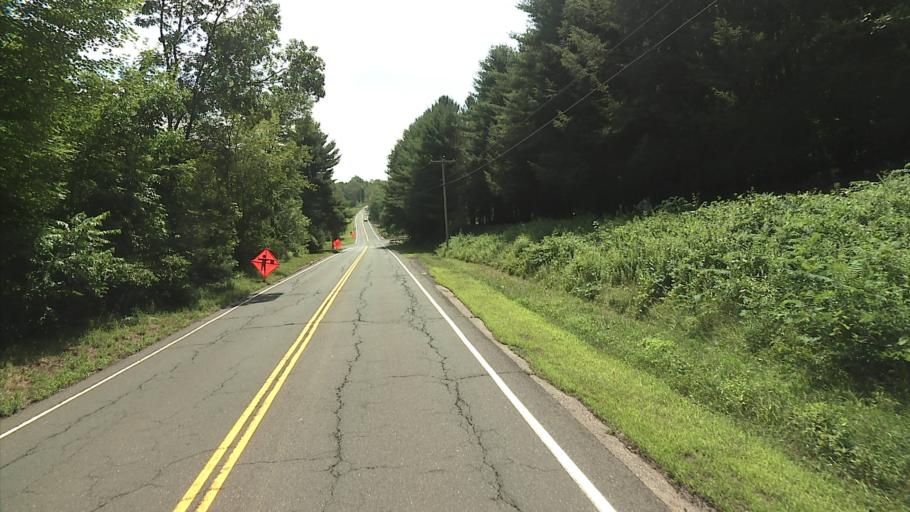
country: US
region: Connecticut
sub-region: Tolland County
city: Coventry Lake
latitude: 41.7926
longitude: -72.3568
